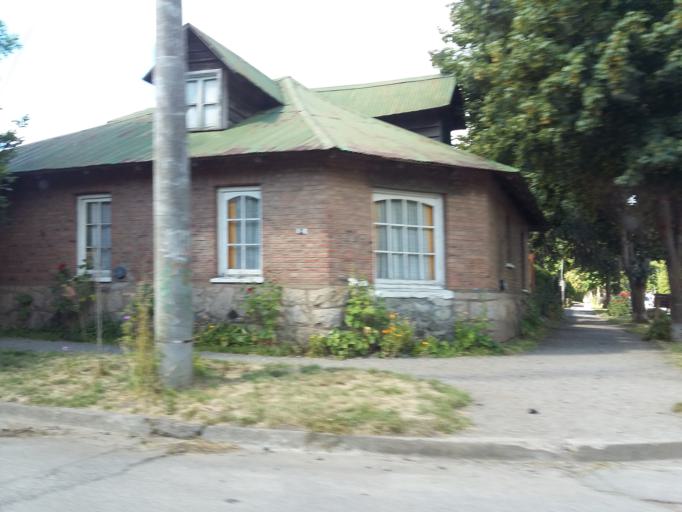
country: AR
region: Neuquen
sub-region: Departamento de Lacar
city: San Martin de los Andes
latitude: -40.1593
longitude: -71.3512
